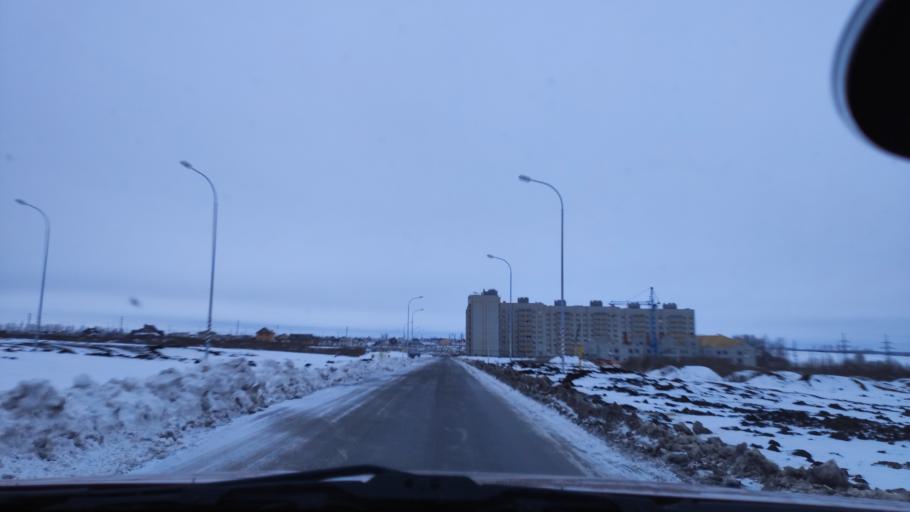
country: RU
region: Tambov
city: Tambov
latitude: 52.7806
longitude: 41.4211
